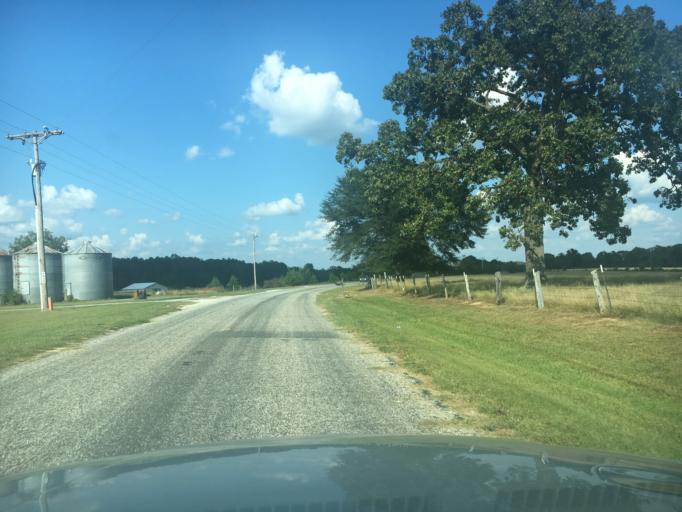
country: US
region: South Carolina
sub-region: Greenwood County
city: Ware Shoals
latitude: 34.4826
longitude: -82.2399
